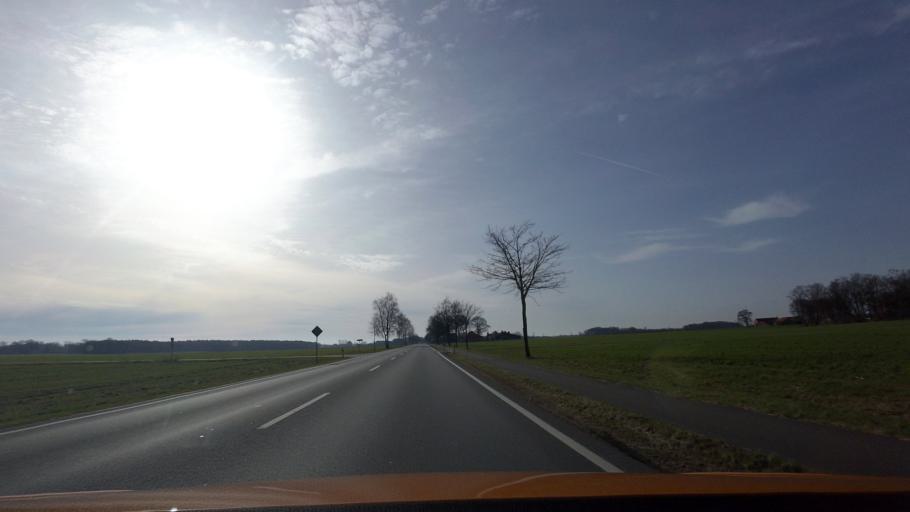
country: DE
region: Lower Saxony
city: Scholen
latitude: 52.7124
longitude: 8.7731
